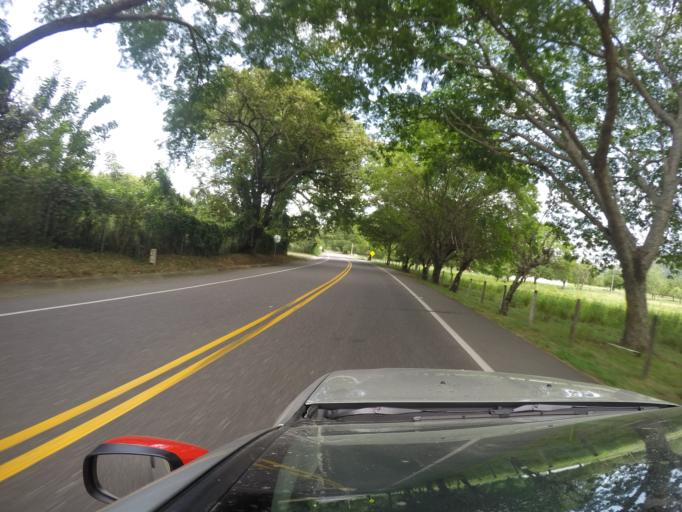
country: CO
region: Tolima
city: Honda
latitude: 5.2800
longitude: -74.7419
